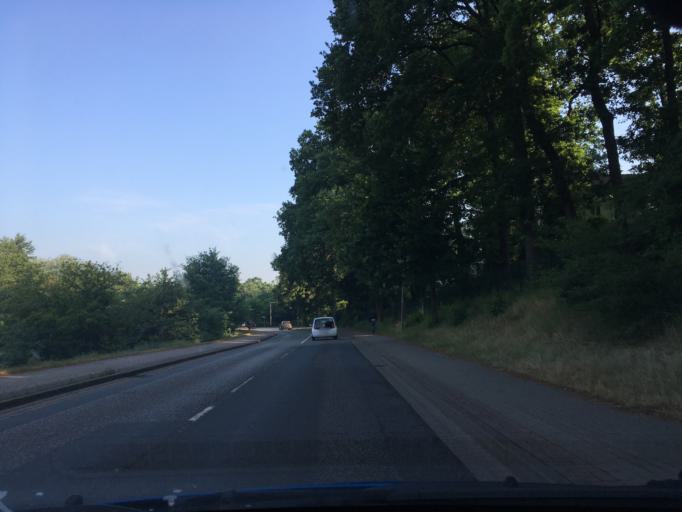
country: DE
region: Lower Saxony
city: Buchholz in der Nordheide
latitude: 53.3407
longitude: 9.8566
